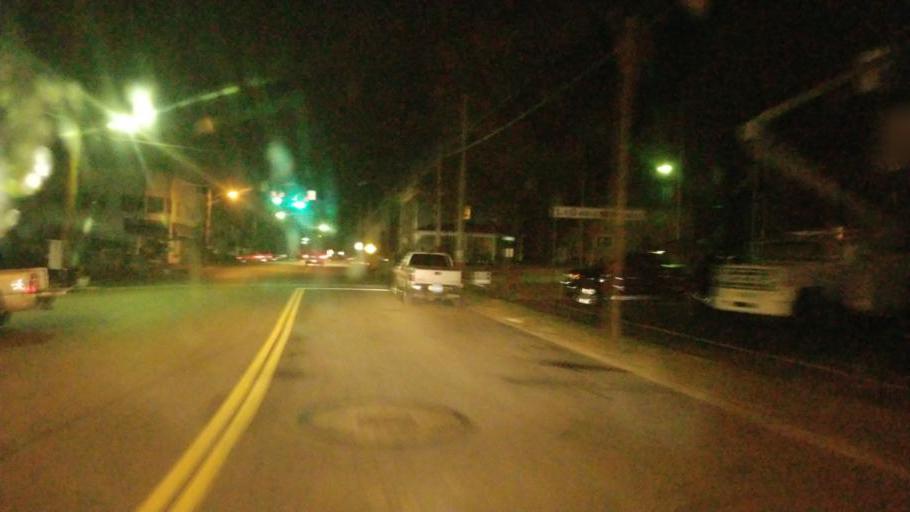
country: US
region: Ohio
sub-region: Ashland County
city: Ashland
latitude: 40.8033
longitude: -82.1952
